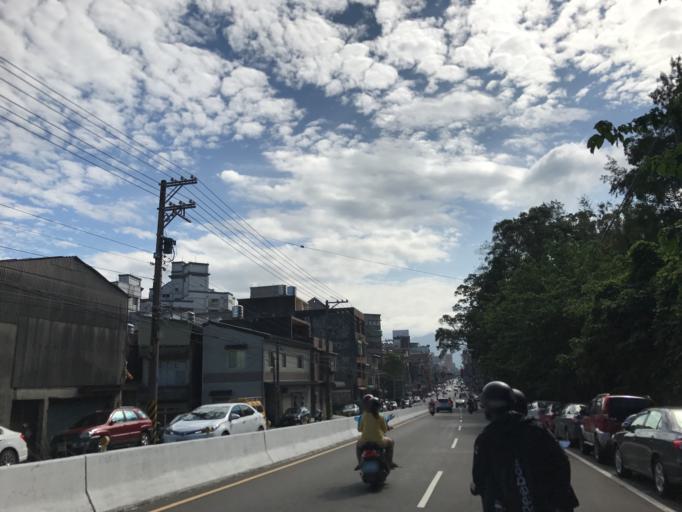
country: TW
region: Taiwan
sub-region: Hsinchu
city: Zhubei
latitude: 24.7485
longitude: 121.0793
